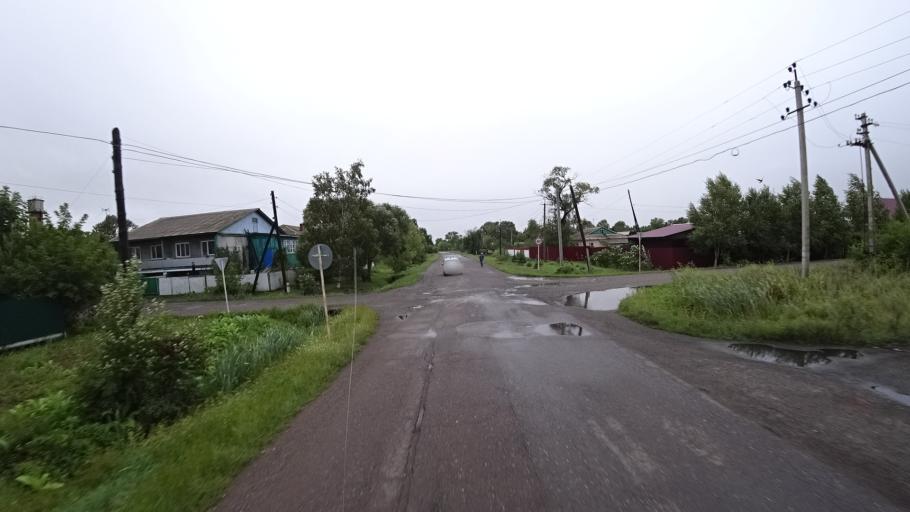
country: RU
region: Primorskiy
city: Chernigovka
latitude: 44.3386
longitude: 132.5744
